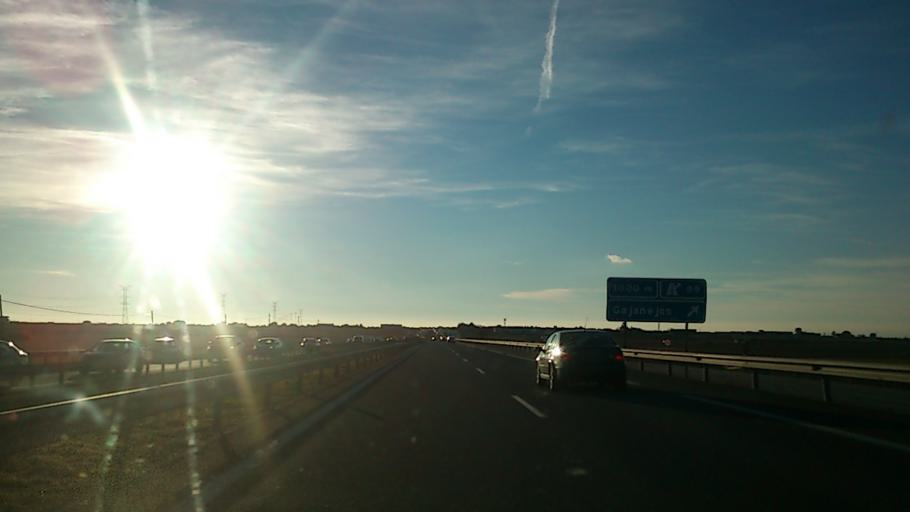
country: ES
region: Castille-La Mancha
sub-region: Provincia de Guadalajara
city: Gajanejos
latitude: 40.8448
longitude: -2.8775
